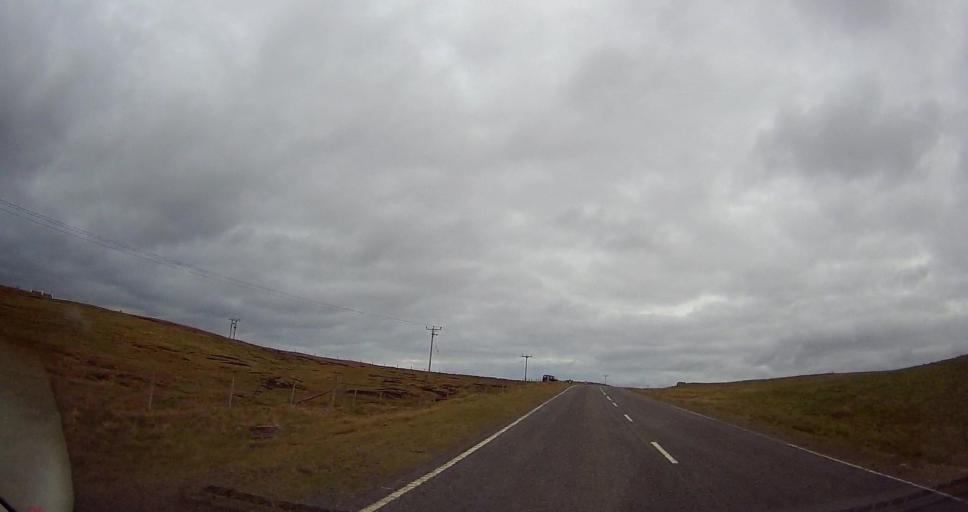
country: GB
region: Scotland
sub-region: Shetland Islands
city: Shetland
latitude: 60.6539
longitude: -1.0678
